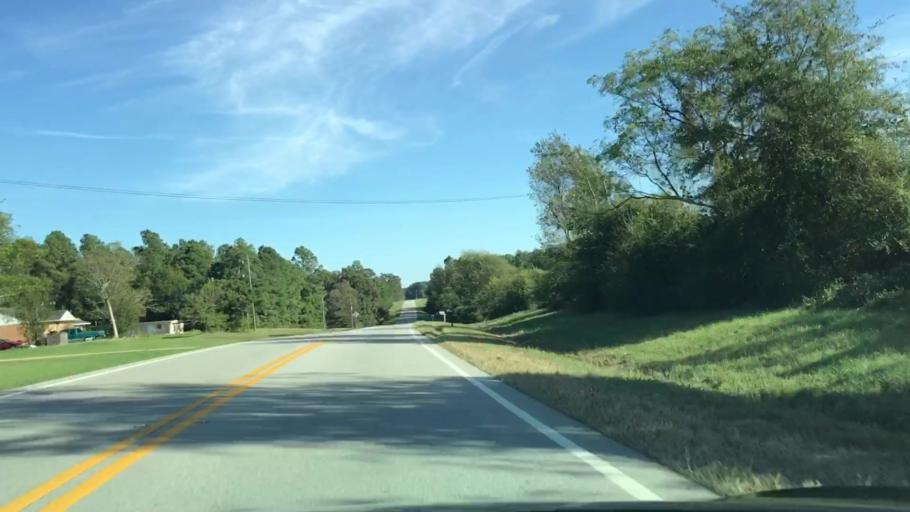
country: US
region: Georgia
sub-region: Glascock County
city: Gibson
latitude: 33.3171
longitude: -82.5472
